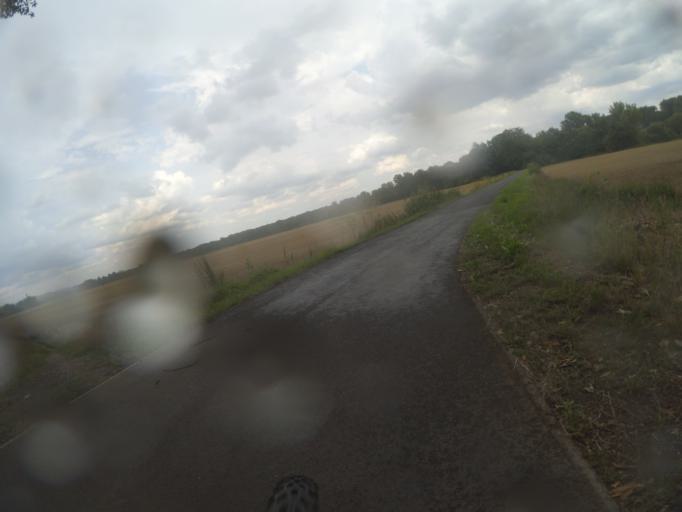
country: CZ
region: Central Bohemia
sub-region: Okres Melnik
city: Melnik
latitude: 50.3253
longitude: 14.4680
